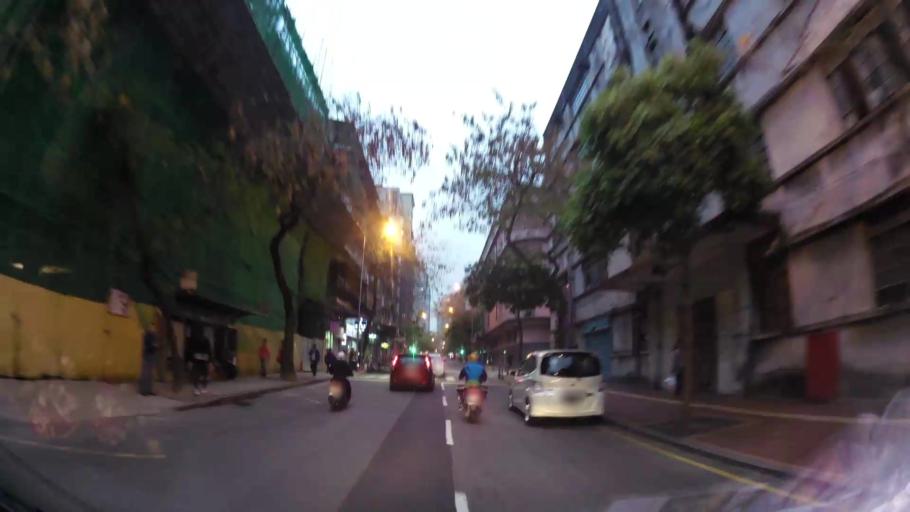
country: MO
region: Macau
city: Macau
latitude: 22.2069
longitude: 113.5463
